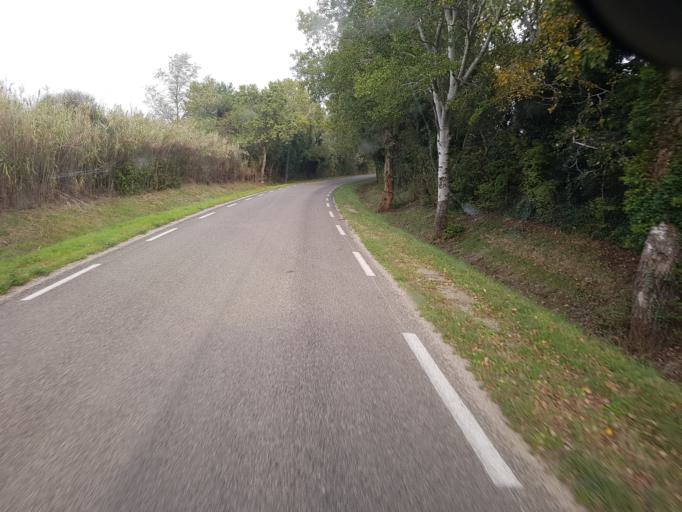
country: FR
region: Languedoc-Roussillon
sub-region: Departement du Gard
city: Aramon
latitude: 43.8715
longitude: 4.6573
